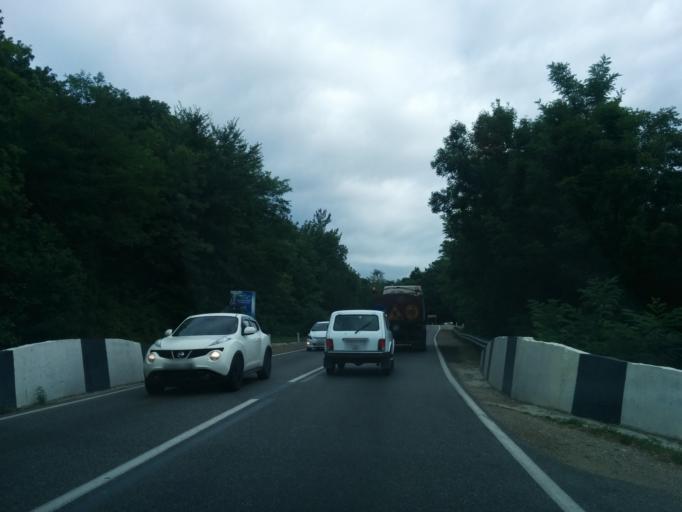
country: RU
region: Krasnodarskiy
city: Agoy
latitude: 44.1273
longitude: 39.0480
